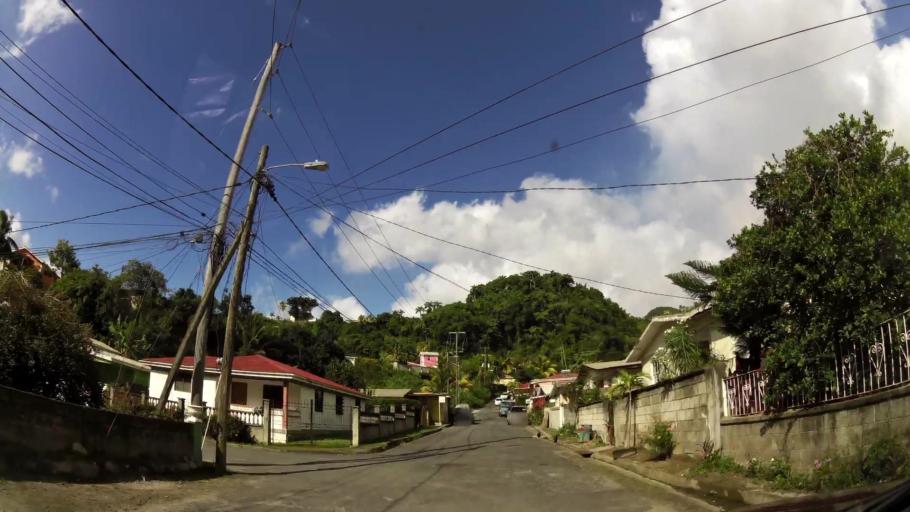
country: DM
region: Saint George
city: Roseau
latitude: 15.3019
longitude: -61.3762
